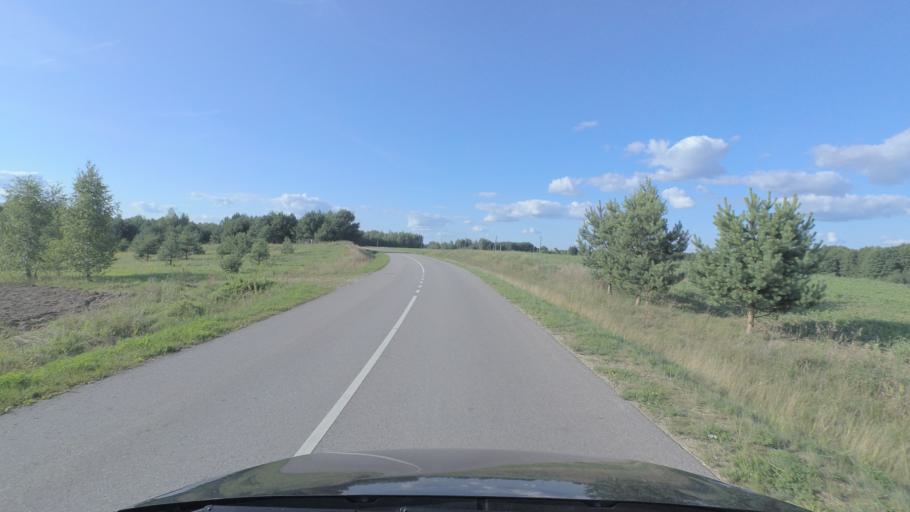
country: LT
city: Pabrade
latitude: 55.0906
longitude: 25.6862
